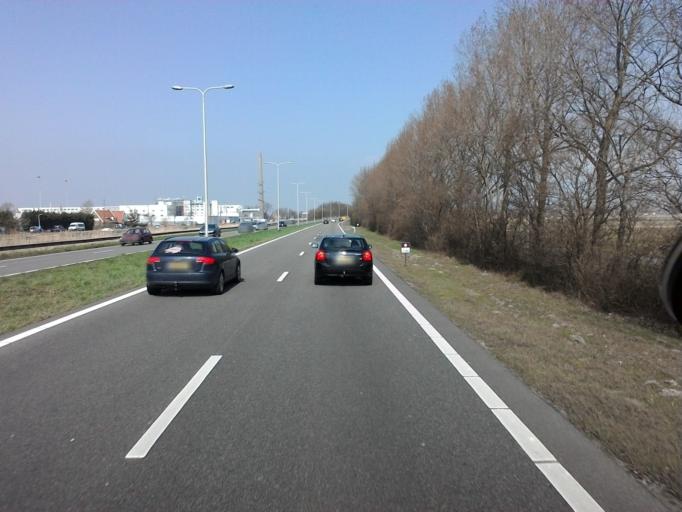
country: NL
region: North Holland
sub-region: Gemeente Zaanstad
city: Zaanstad
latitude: 52.4865
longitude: 4.7718
